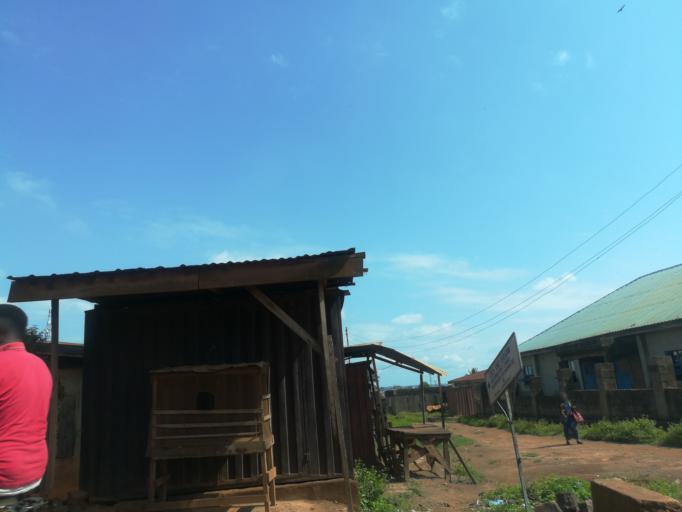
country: NG
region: Oyo
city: Egbeda
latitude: 7.4153
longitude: 3.9918
